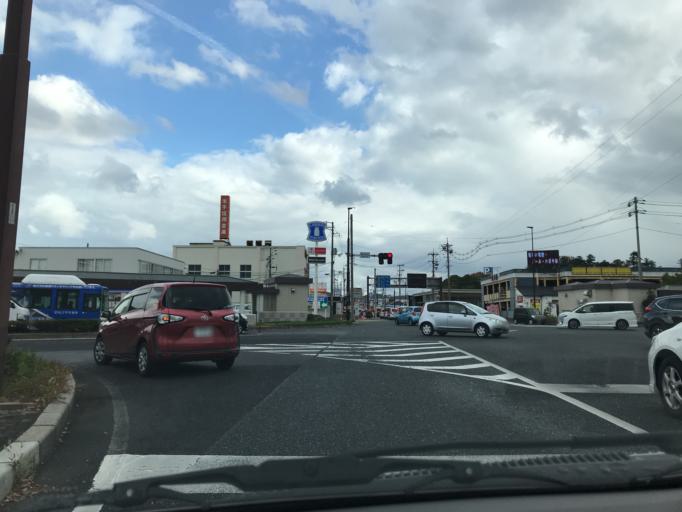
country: JP
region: Shimane
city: Matsue-shi
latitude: 35.4589
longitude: 133.0662
